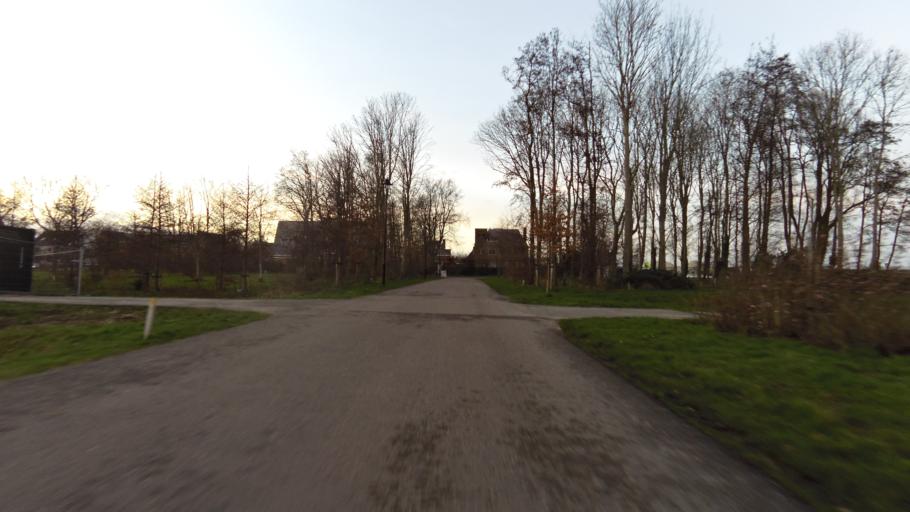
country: NL
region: South Holland
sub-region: Gemeente Noordwijkerhout
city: Noordwijkerhout
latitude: 52.2788
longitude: 4.4954
